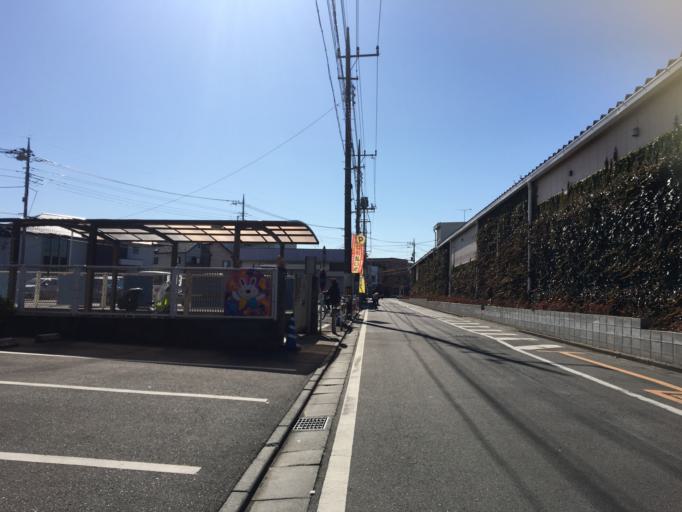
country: JP
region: Saitama
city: Kamifukuoka
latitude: 35.8661
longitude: 139.5106
